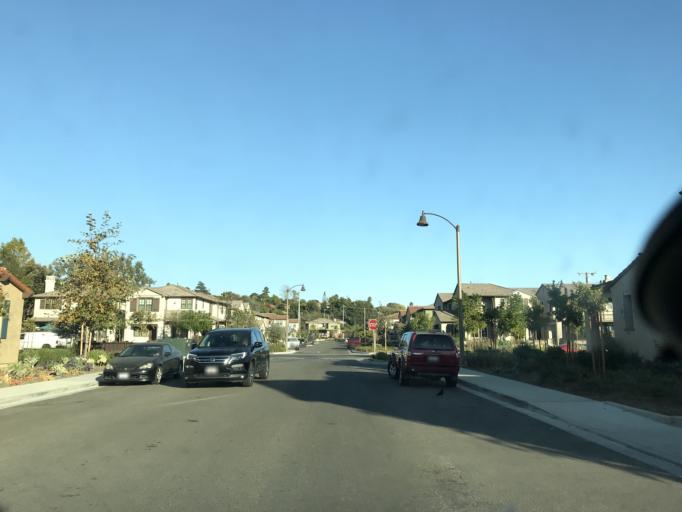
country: US
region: California
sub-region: Santa Barbara County
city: Goleta
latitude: 34.4490
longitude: -119.8115
